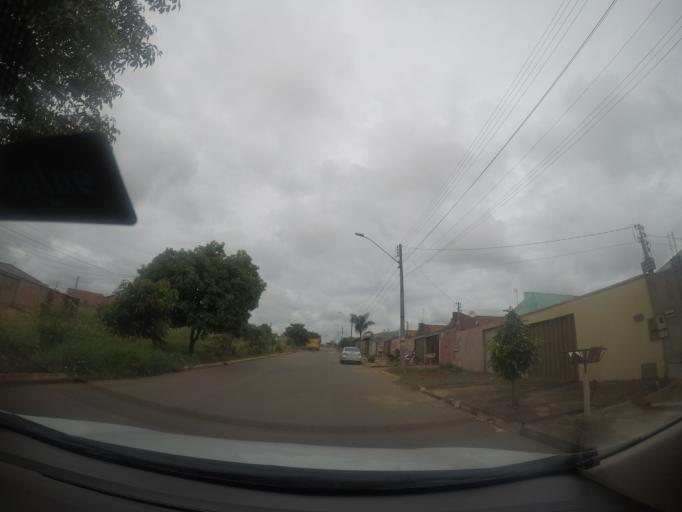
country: BR
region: Goias
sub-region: Trindade
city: Trindade
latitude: -16.6869
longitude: -49.4038
